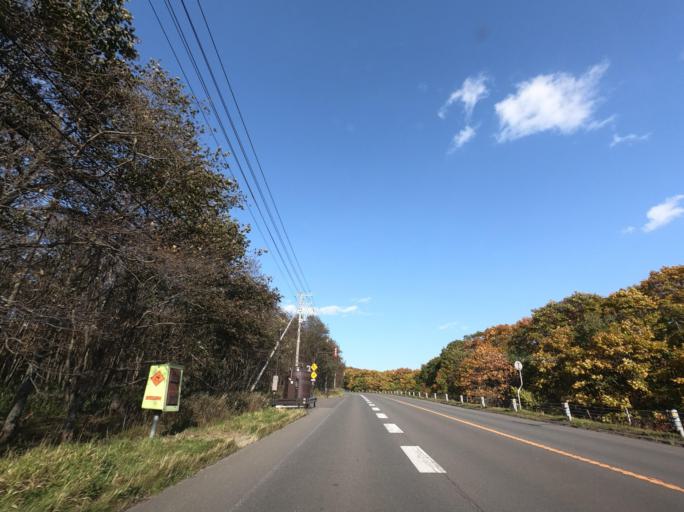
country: JP
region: Hokkaido
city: Kushiro
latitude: 43.0695
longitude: 144.3176
